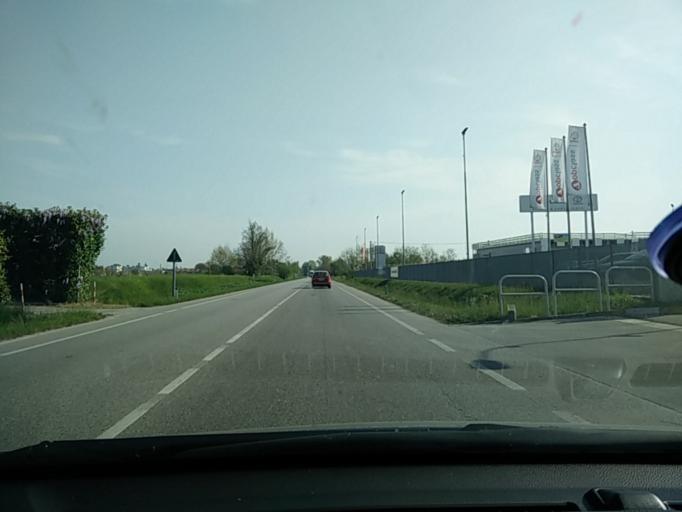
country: IT
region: Friuli Venezia Giulia
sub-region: Provincia di Pordenone
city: Azzano Decimo
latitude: 45.9225
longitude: 12.6375
